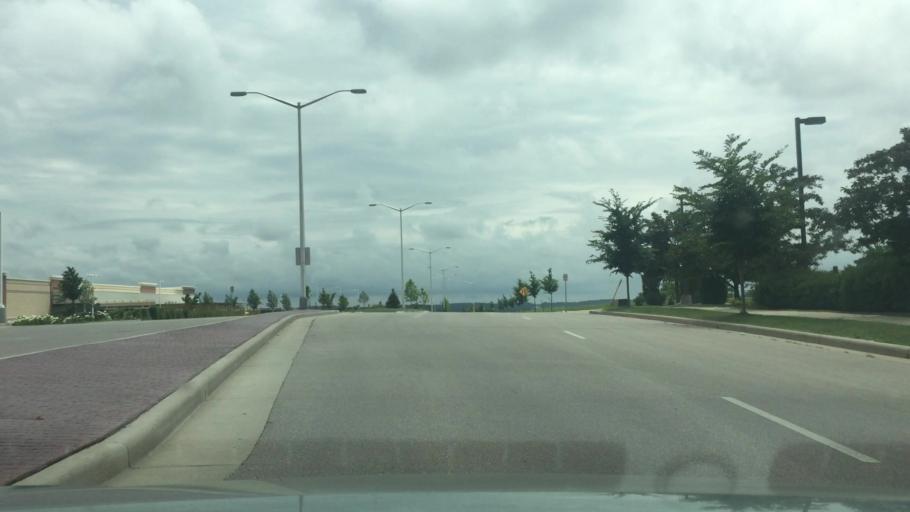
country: US
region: Wisconsin
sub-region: Waukesha County
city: Waukesha
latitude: 42.9878
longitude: -88.2211
